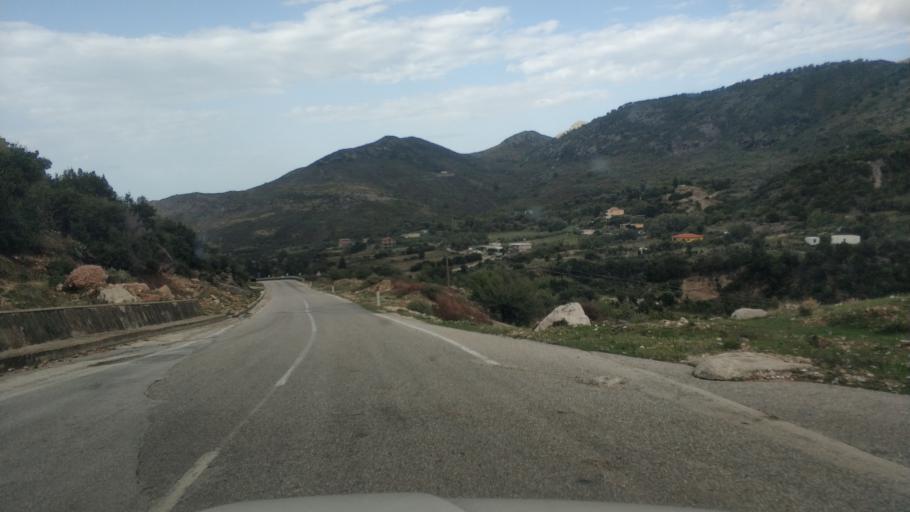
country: AL
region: Vlore
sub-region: Rrethi i Vlores
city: Orikum
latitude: 40.2665
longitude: 19.5159
